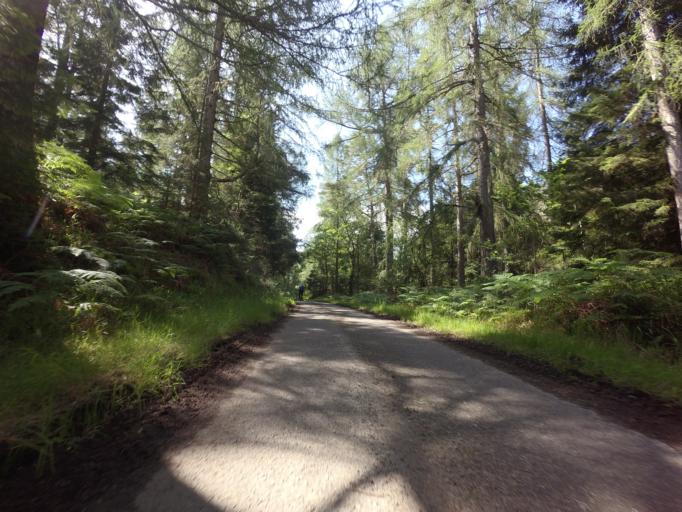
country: GB
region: Scotland
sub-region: Highland
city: Nairn
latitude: 57.5050
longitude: -3.9094
